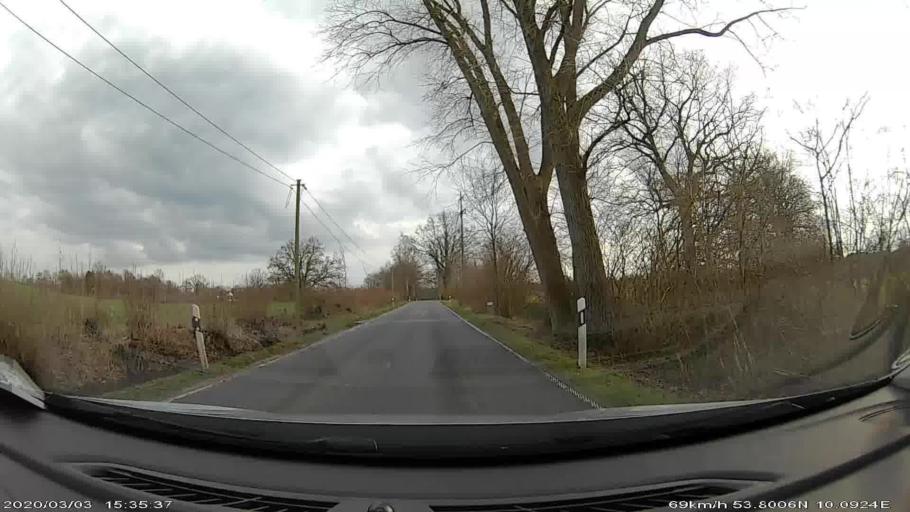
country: DE
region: Schleswig-Holstein
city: Huttblek
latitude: 53.8014
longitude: 10.0921
